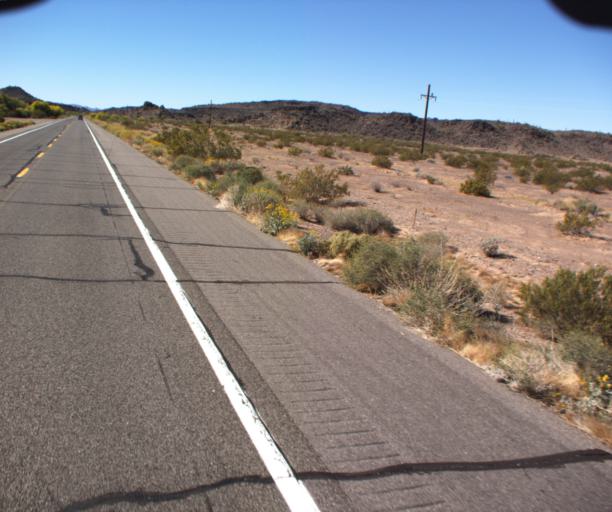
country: US
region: Arizona
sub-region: Pima County
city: Ajo
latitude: 32.5745
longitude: -112.8749
